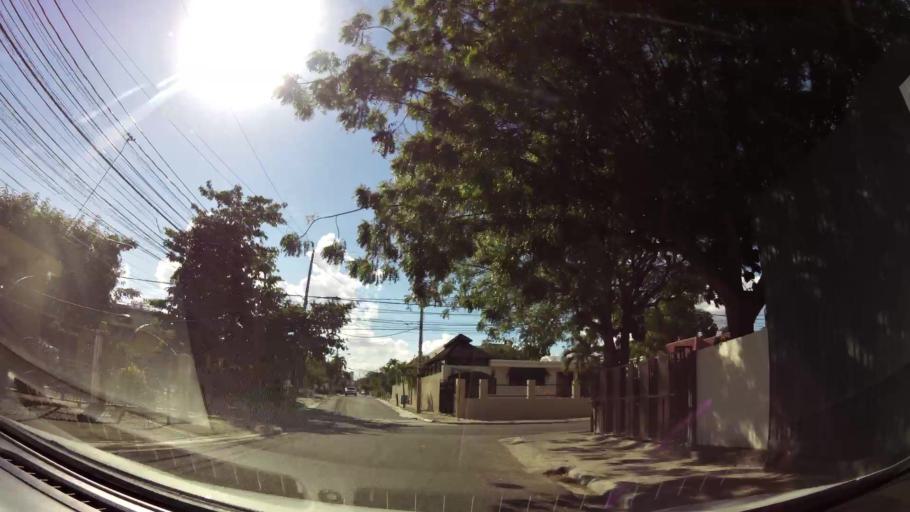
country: DO
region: Santiago
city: Santiago de los Caballeros
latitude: 19.4526
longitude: -70.6711
